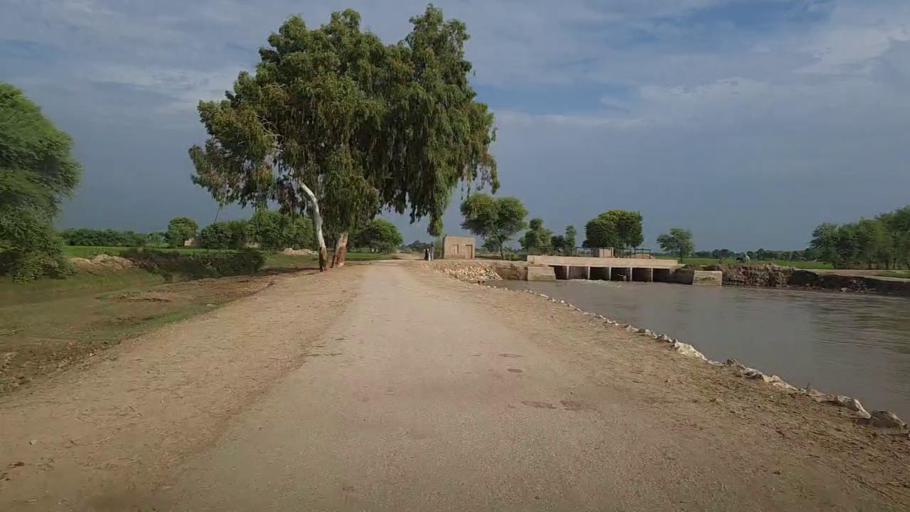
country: PK
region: Sindh
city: Thul
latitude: 28.2542
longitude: 68.8579
